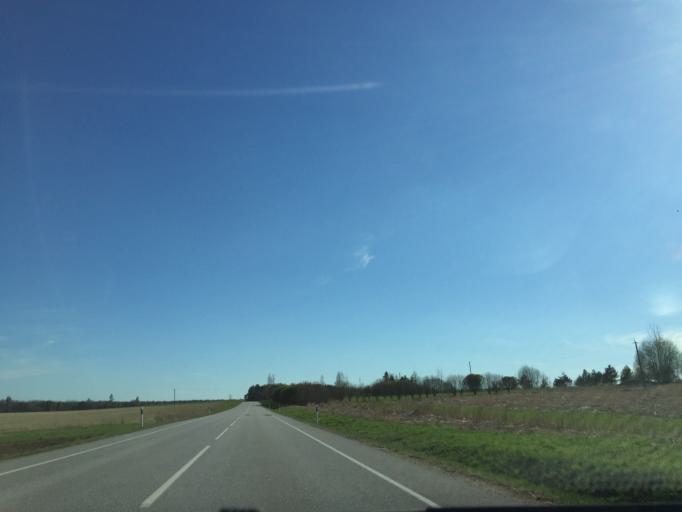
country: EE
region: Vorumaa
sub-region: Antsla vald
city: Vana-Antsla
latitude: 57.8798
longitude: 26.2804
